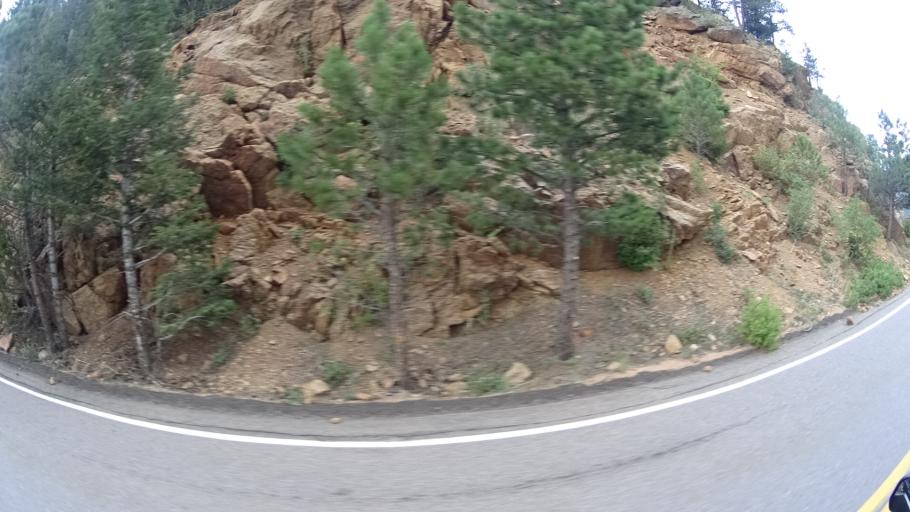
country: US
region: Colorado
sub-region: El Paso County
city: Cascade-Chipita Park
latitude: 38.8968
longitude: -104.9856
